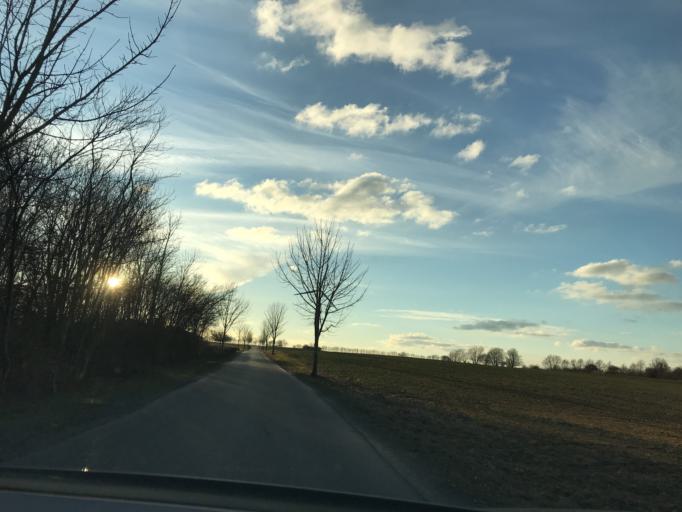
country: DK
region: South Denmark
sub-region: Middelfart Kommune
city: Ejby
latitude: 55.4639
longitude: 9.9427
